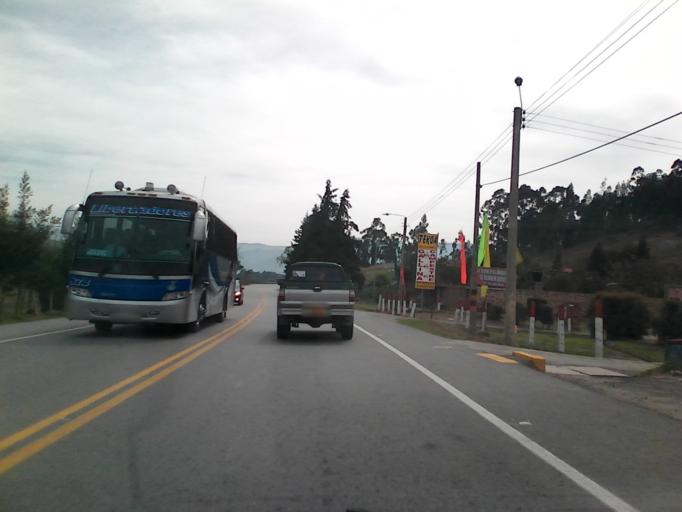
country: CO
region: Boyaca
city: Tibasosa
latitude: 5.7438
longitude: -72.9824
